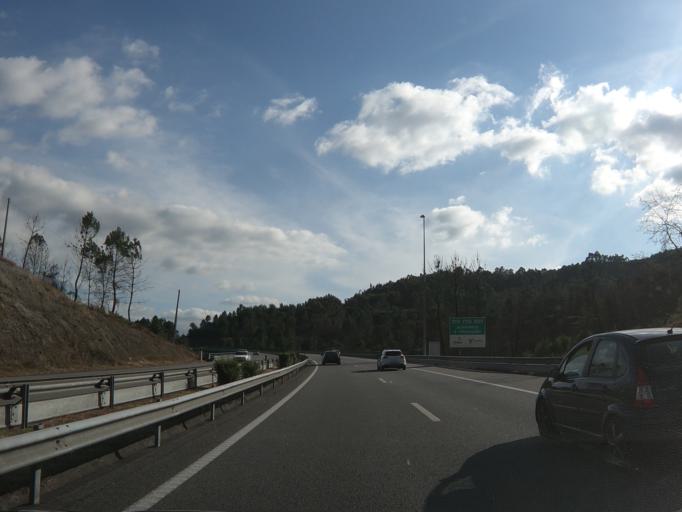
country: PT
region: Porto
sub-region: Amarante
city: Amarante
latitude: 41.2398
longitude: -8.1188
